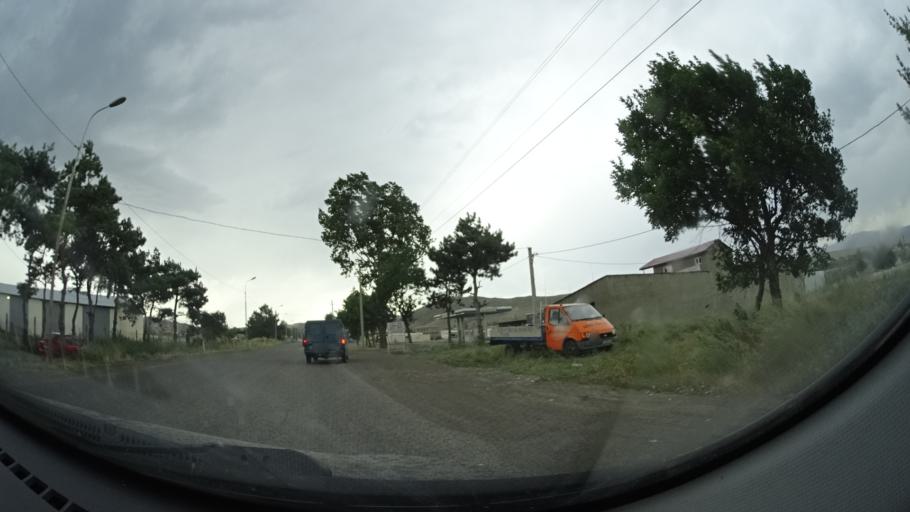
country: GE
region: Samtskhe-Javakheti
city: Akhaltsikhe
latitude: 41.6426
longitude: 43.0105
